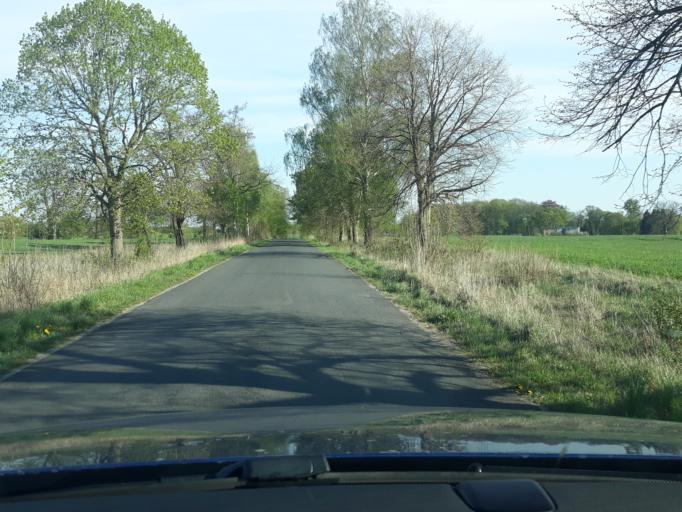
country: PL
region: Pomeranian Voivodeship
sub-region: Powiat czluchowski
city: Przechlewo
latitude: 53.8494
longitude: 17.3559
